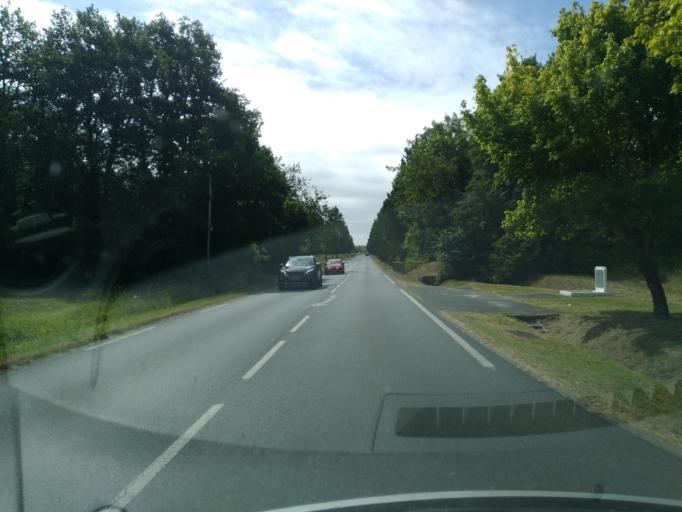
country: FR
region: Poitou-Charentes
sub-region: Departement de la Charente-Maritime
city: Chaillevette
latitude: 45.7133
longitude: -1.0669
